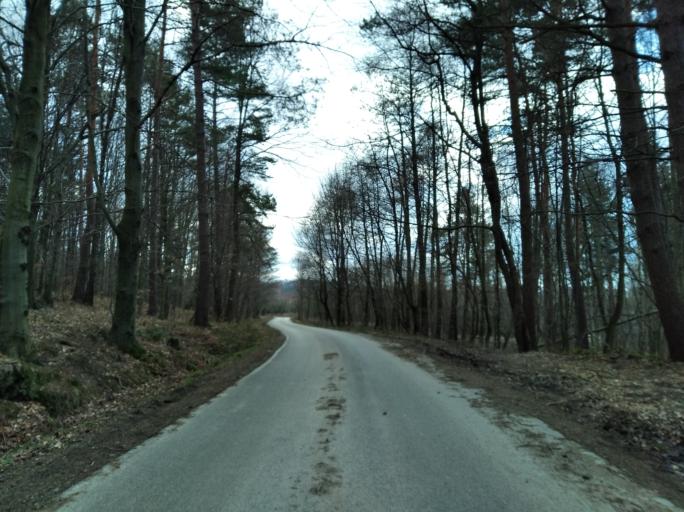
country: PL
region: Subcarpathian Voivodeship
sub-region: Powiat strzyzowski
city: Wysoka Strzyzowska
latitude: 49.7973
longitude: 21.7282
